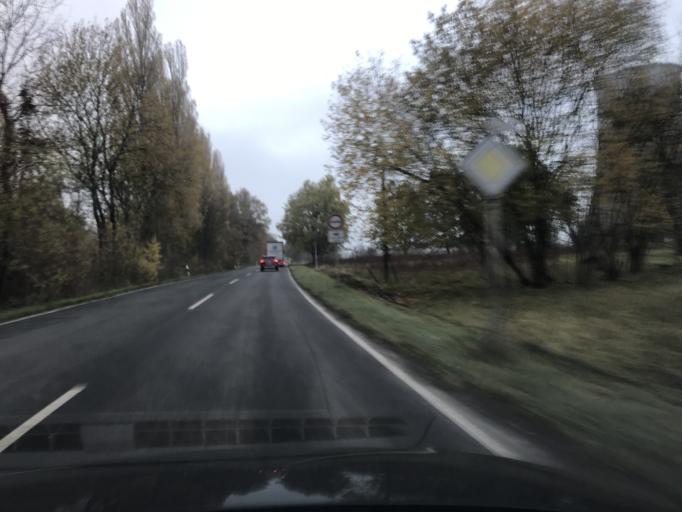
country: DE
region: North Rhine-Westphalia
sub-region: Regierungsbezirk Arnsberg
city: Welver
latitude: 51.6800
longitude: 7.9767
